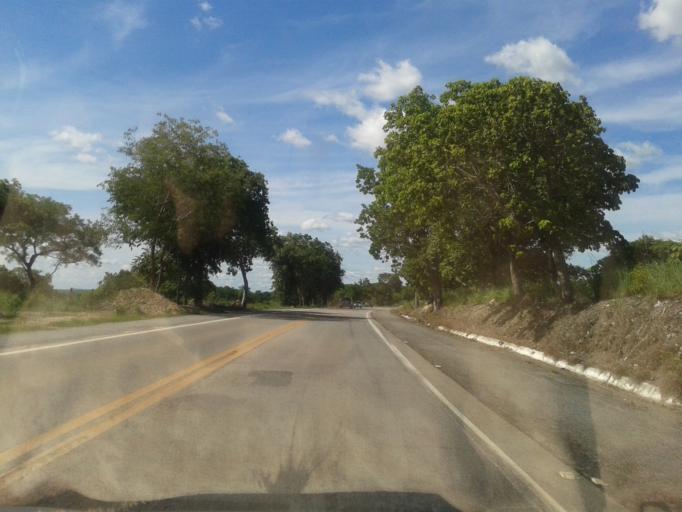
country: BR
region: Goias
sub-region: Itapuranga
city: Itapuranga
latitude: -15.4226
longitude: -50.3763
